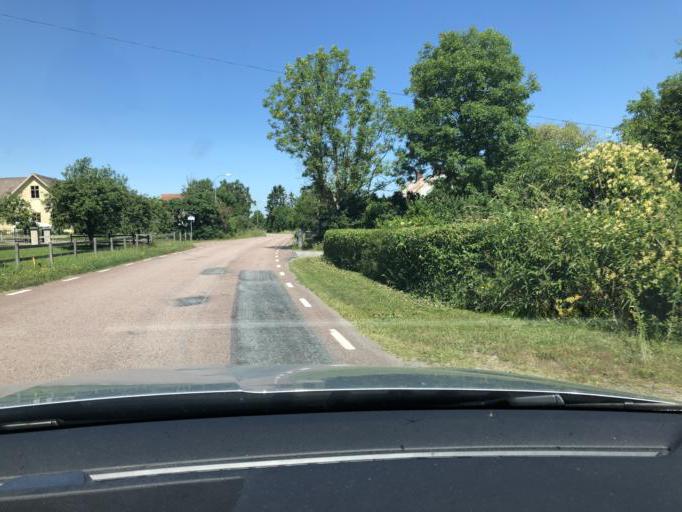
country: SE
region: Blekinge
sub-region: Solvesborgs Kommun
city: Soelvesborg
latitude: 56.1471
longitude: 14.6033
